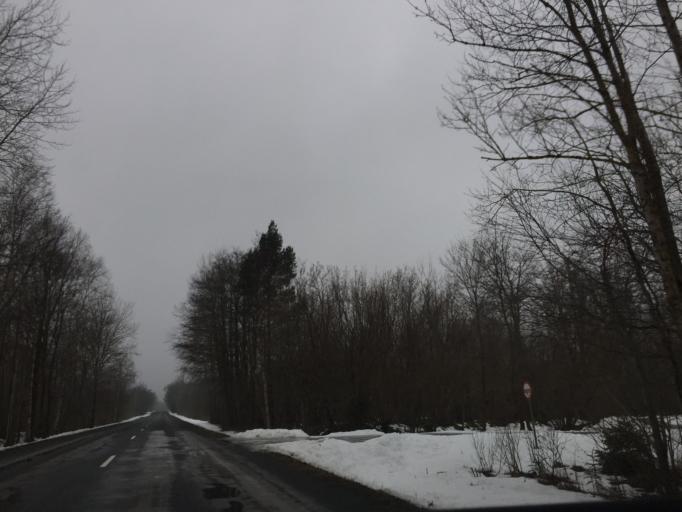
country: EE
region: Saare
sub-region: Orissaare vald
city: Orissaare
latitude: 58.3924
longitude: 22.8511
